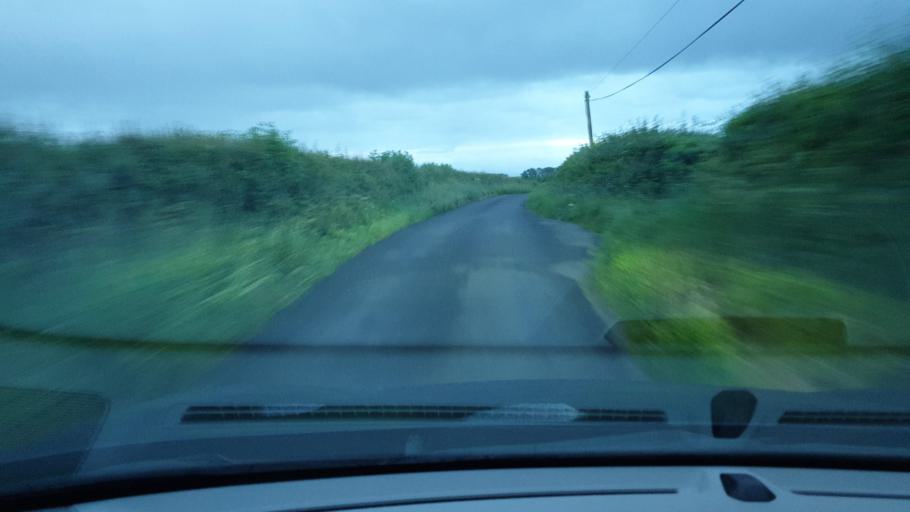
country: IE
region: Leinster
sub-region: An Mhi
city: Ashbourne
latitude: 53.5088
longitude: -6.3600
